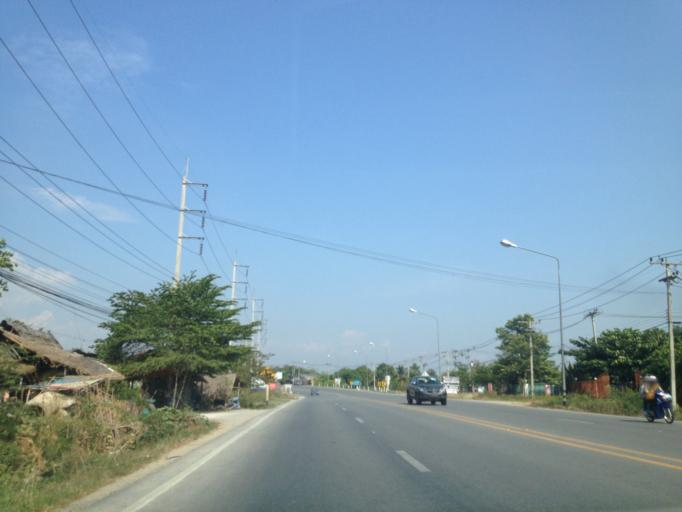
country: TH
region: Chiang Mai
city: Chom Thong
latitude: 18.3451
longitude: 98.6800
